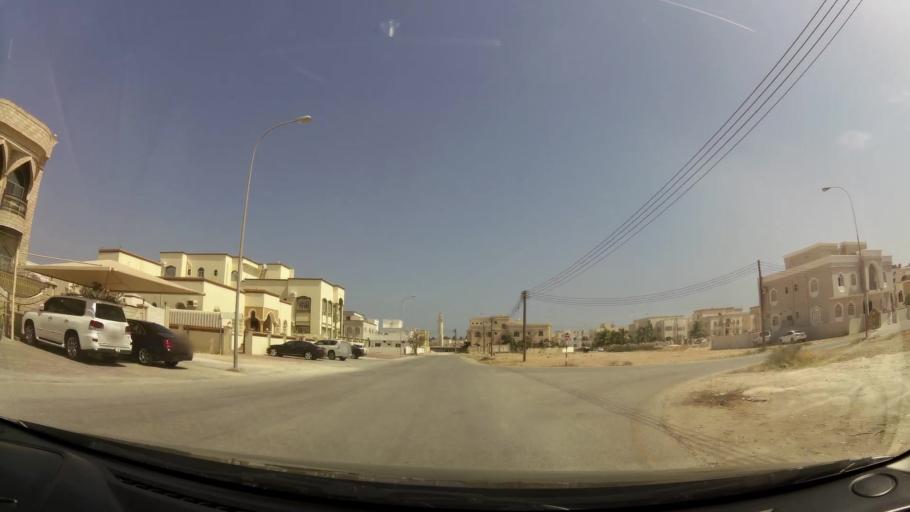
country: OM
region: Zufar
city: Salalah
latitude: 17.0427
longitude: 54.1575
